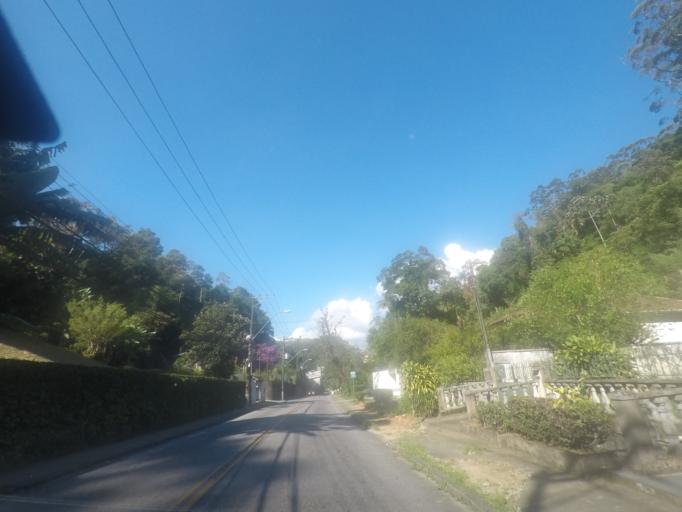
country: BR
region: Rio de Janeiro
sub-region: Petropolis
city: Petropolis
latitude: -22.5270
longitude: -43.1881
